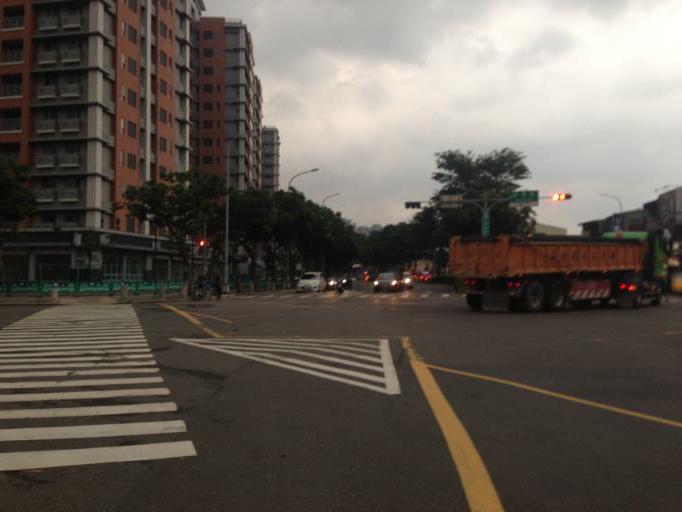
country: TW
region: Taiwan
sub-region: Taoyuan
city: Taoyuan
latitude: 24.9378
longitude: 121.3777
